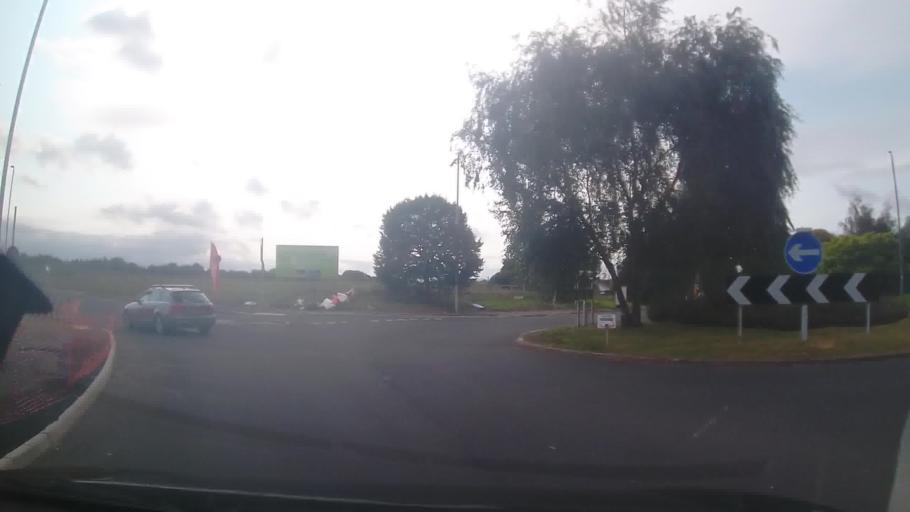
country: GB
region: England
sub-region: Shropshire
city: Shrewsbury
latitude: 52.6907
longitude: -2.7165
